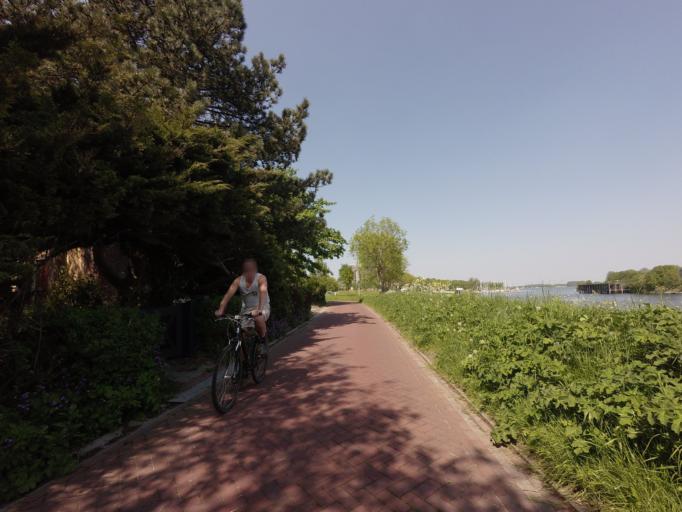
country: NL
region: Zeeland
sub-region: Gemeente Veere
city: Veere
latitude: 51.5430
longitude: 3.6667
